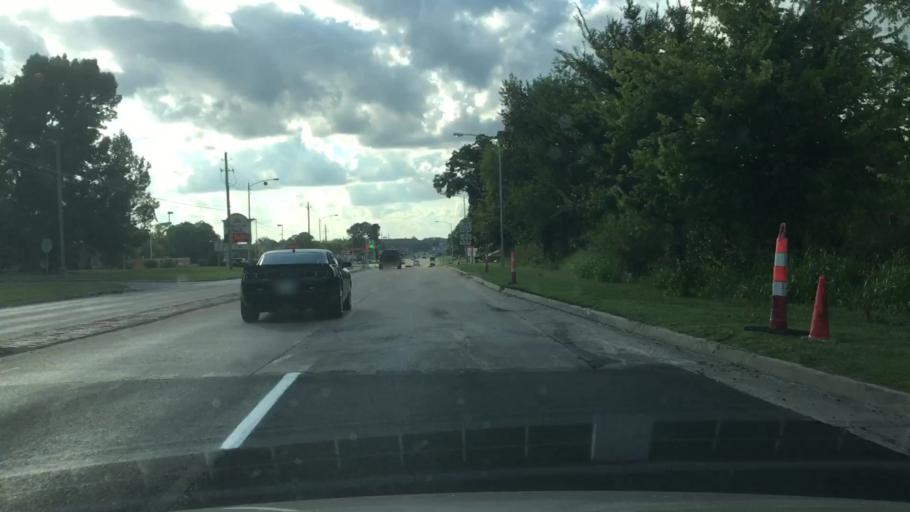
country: US
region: Oklahoma
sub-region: Cherokee County
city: Tahlequah
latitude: 35.9154
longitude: -94.9500
